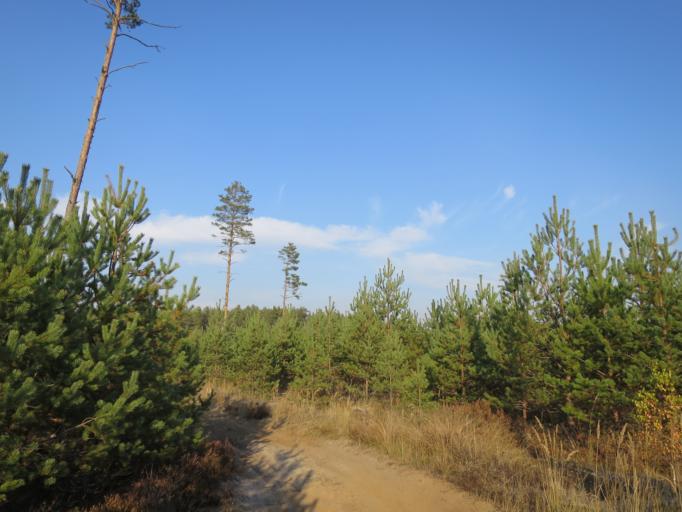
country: LV
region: Incukalns
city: Vangazi
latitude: 57.0397
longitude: 24.5114
